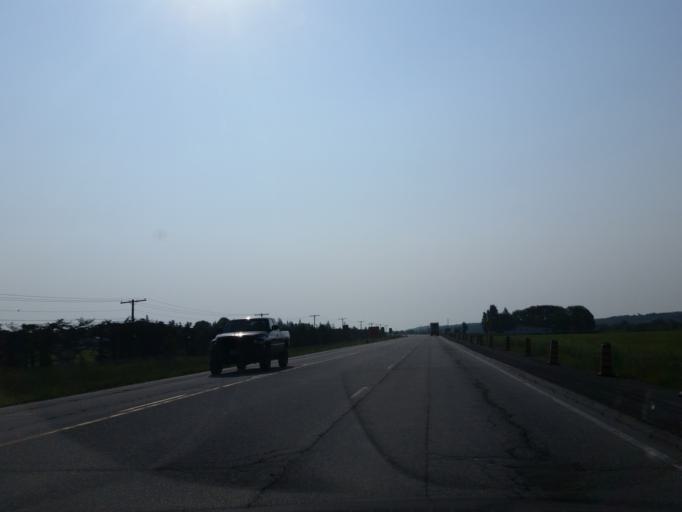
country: CA
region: Ontario
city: Greater Sudbury
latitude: 46.4320
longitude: -80.2555
